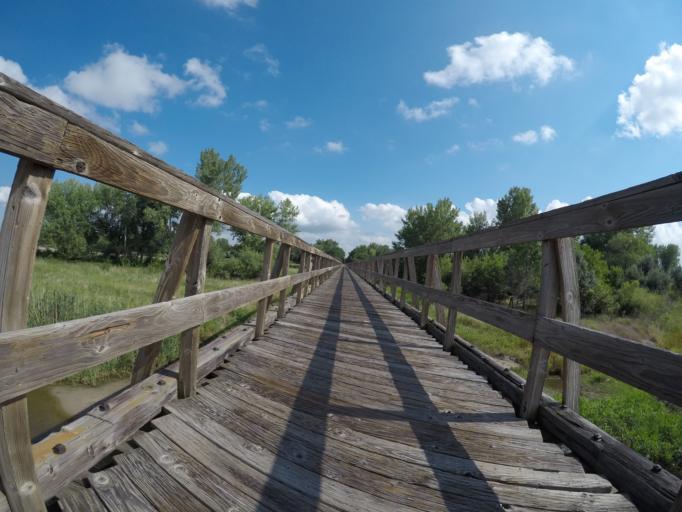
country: US
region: Nebraska
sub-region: Buffalo County
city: Kearney
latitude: 40.6618
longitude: -98.9878
